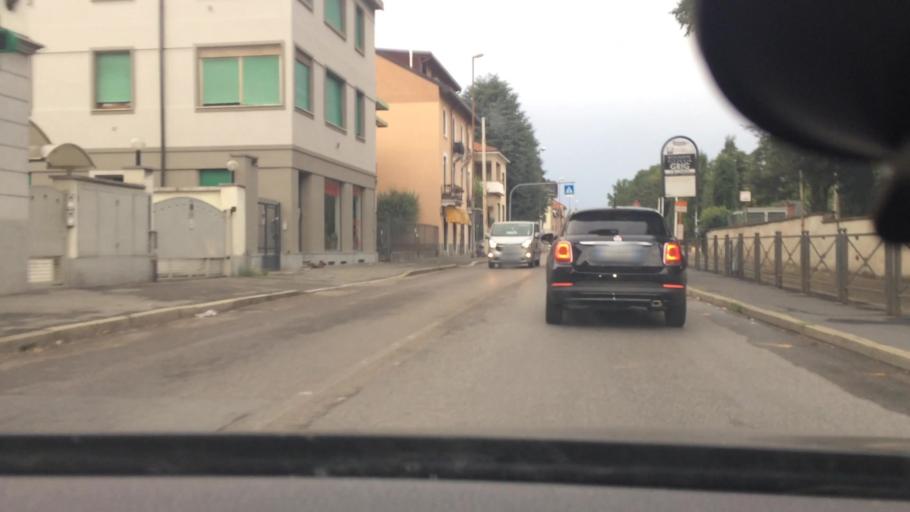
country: IT
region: Lombardy
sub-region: Provincia di Monza e Brianza
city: Nova Milanese
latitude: 45.5890
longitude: 9.1969
